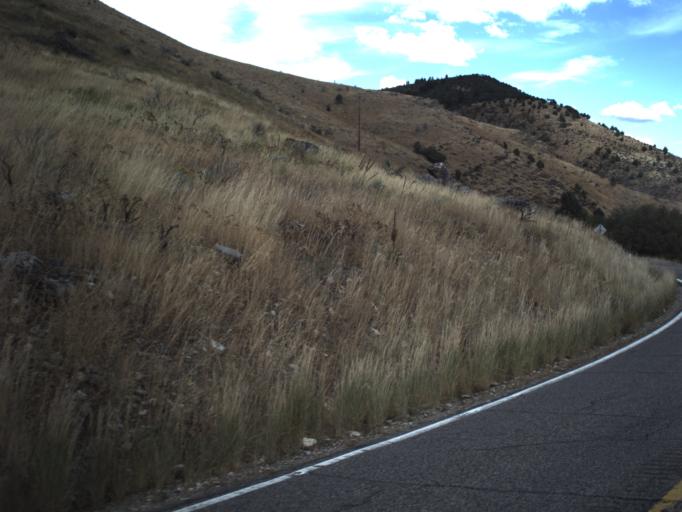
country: US
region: Utah
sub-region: Cache County
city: Millville
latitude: 41.6169
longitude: -111.6442
